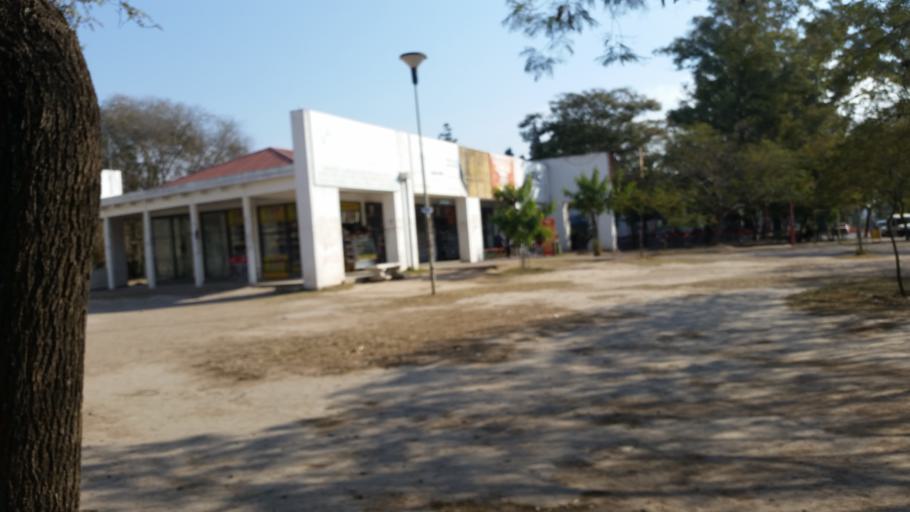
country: AR
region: Cordoba
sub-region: Departamento de Capital
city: Cordoba
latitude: -31.4379
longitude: -64.1914
